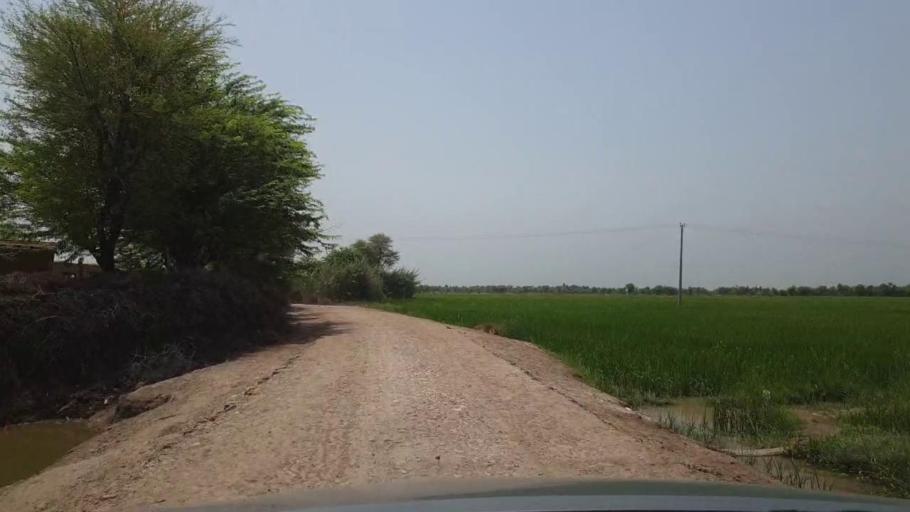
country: PK
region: Sindh
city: Madeji
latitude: 27.7748
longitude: 68.4055
